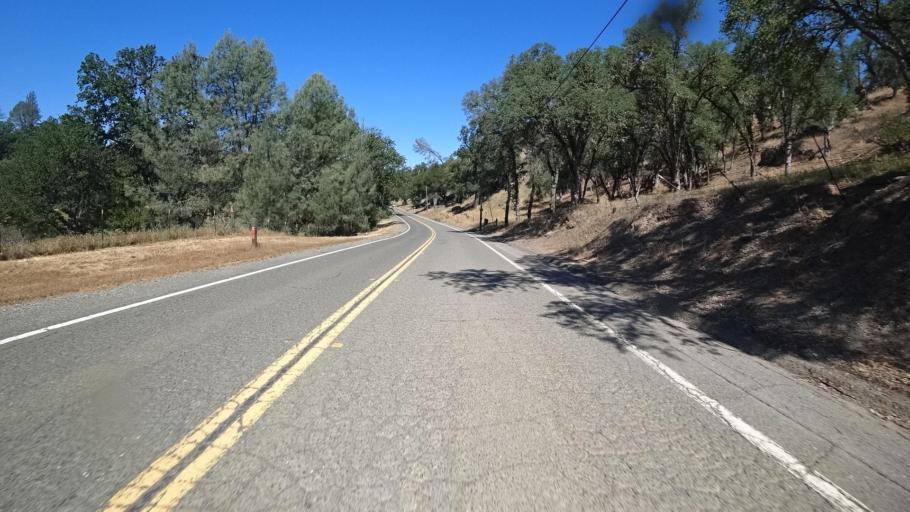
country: US
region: California
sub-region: Lake County
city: Lower Lake
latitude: 38.9016
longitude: -122.5715
